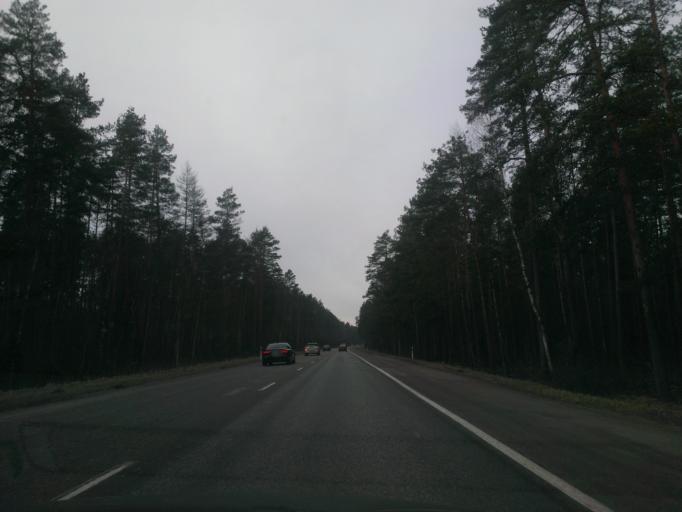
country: LV
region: Incukalns
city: Vangazi
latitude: 57.0759
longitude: 24.5072
